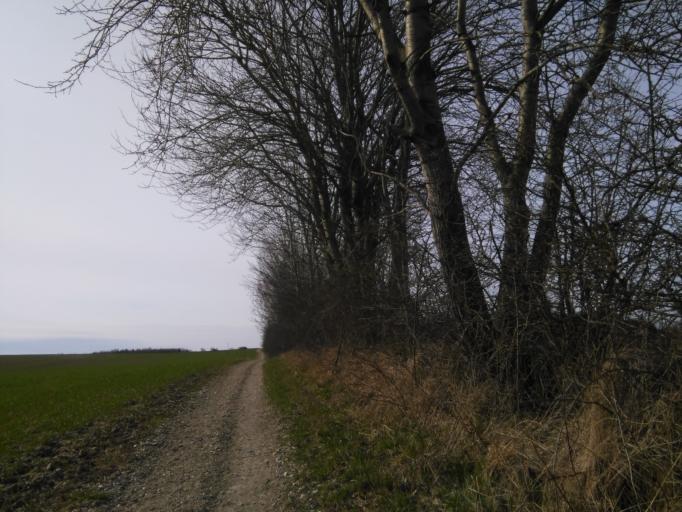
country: DK
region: Central Jutland
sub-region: Arhus Kommune
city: Beder
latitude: 56.0705
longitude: 10.2358
